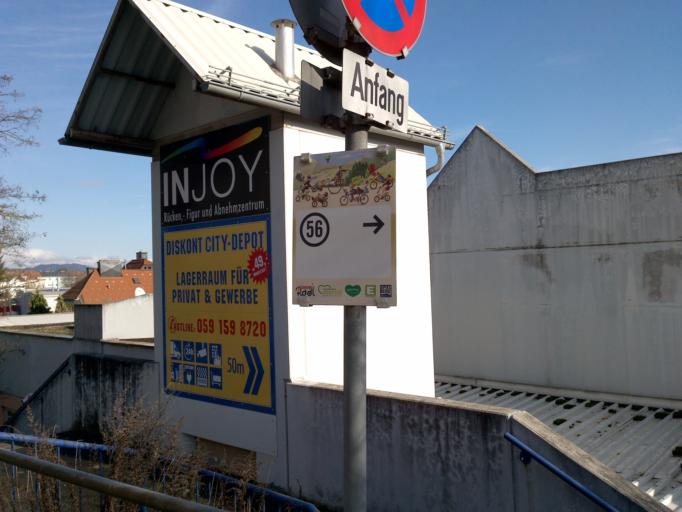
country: AT
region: Styria
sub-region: Politischer Bezirk Murtal
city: Apfelberg
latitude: 47.2134
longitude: 14.8312
